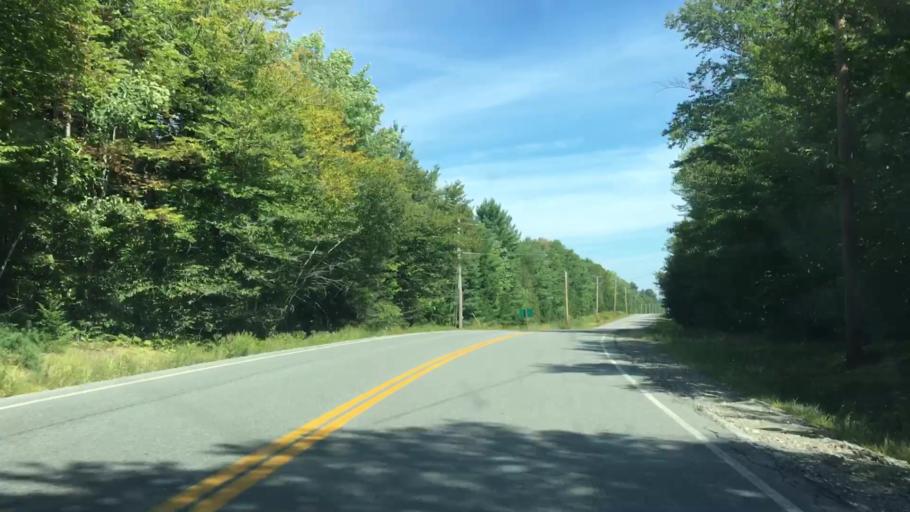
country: US
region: Maine
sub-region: Penobscot County
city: Howland
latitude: 45.2302
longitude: -68.7725
